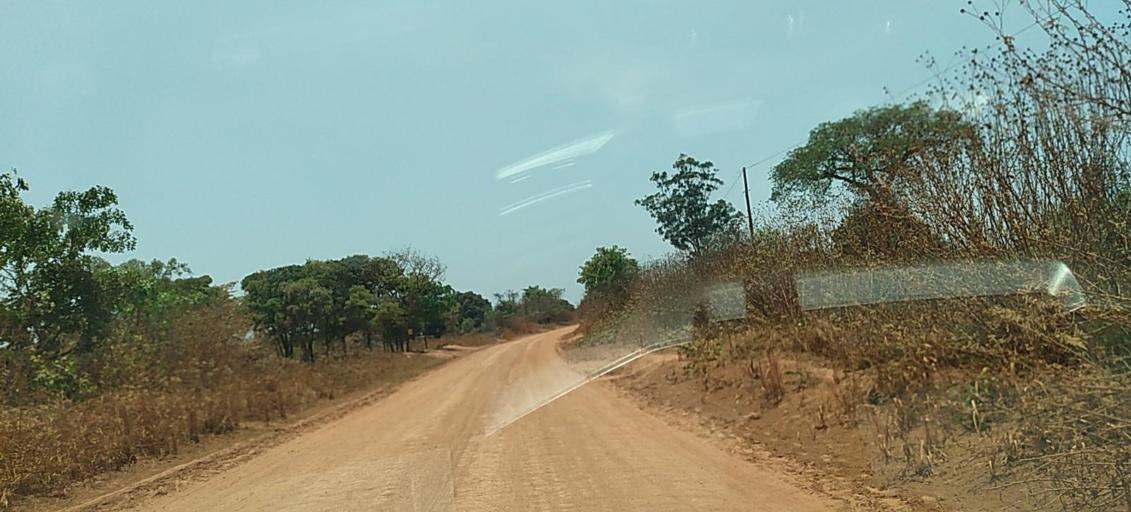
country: CD
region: Katanga
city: Kipushi
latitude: -11.7830
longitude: 27.1787
